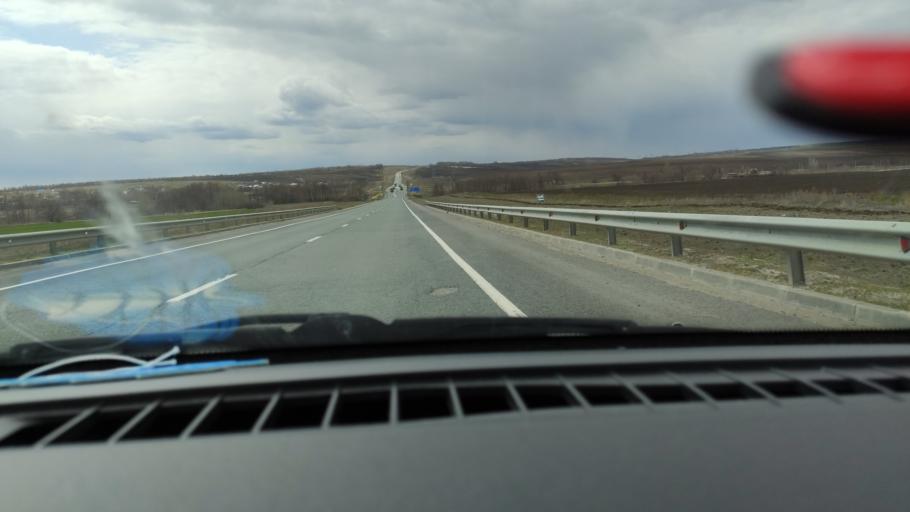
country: RU
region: Saratov
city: Yelshanka
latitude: 51.8260
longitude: 46.3907
